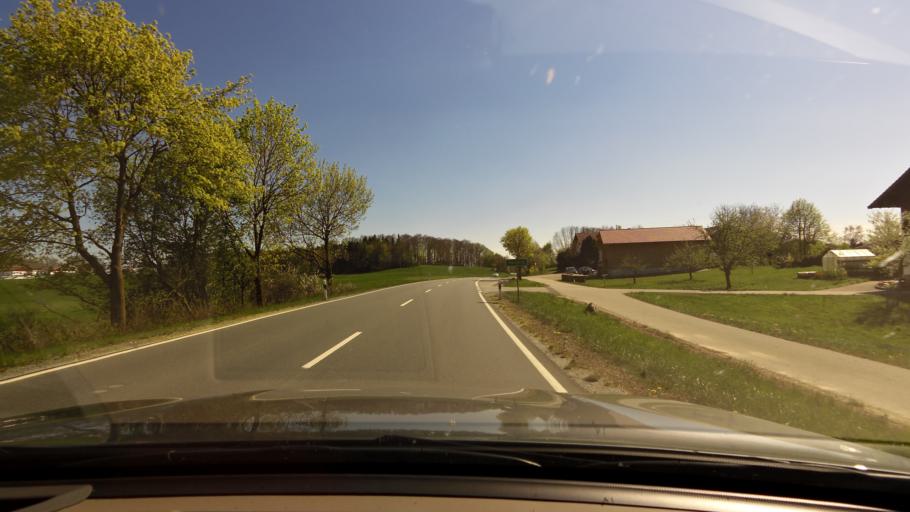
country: DE
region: Bavaria
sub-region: Upper Bavaria
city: Altdorf
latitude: 48.1391
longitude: 12.1874
